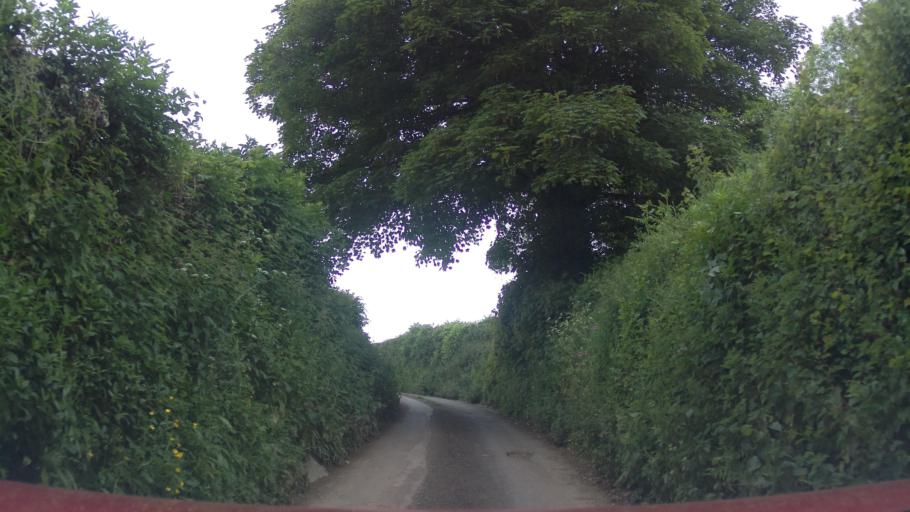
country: GB
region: England
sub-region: Devon
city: Dartmouth
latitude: 50.3198
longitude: -3.6177
